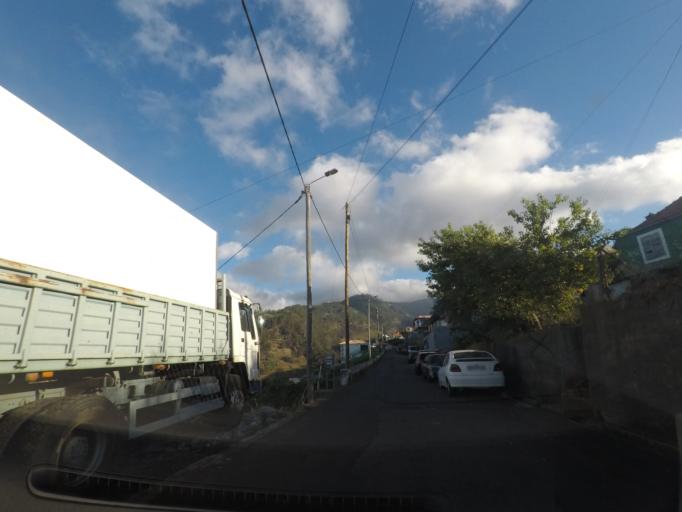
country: PT
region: Madeira
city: Ponta do Sol
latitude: 32.6910
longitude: -17.0878
